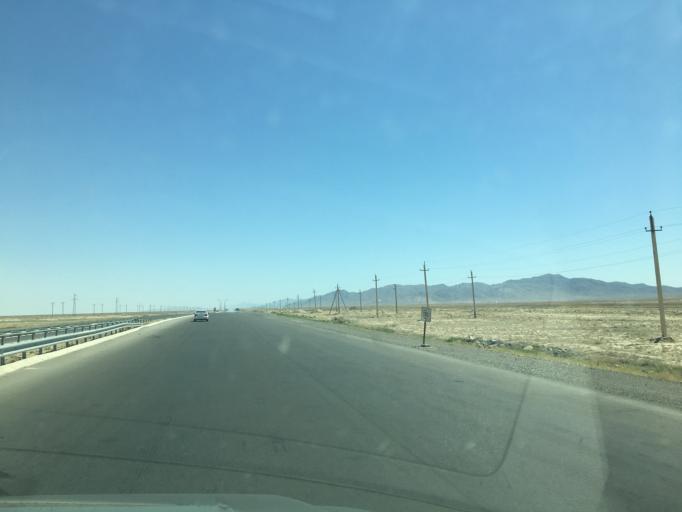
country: TM
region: Balkan
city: Gazanjyk
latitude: 39.1304
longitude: 55.8902
